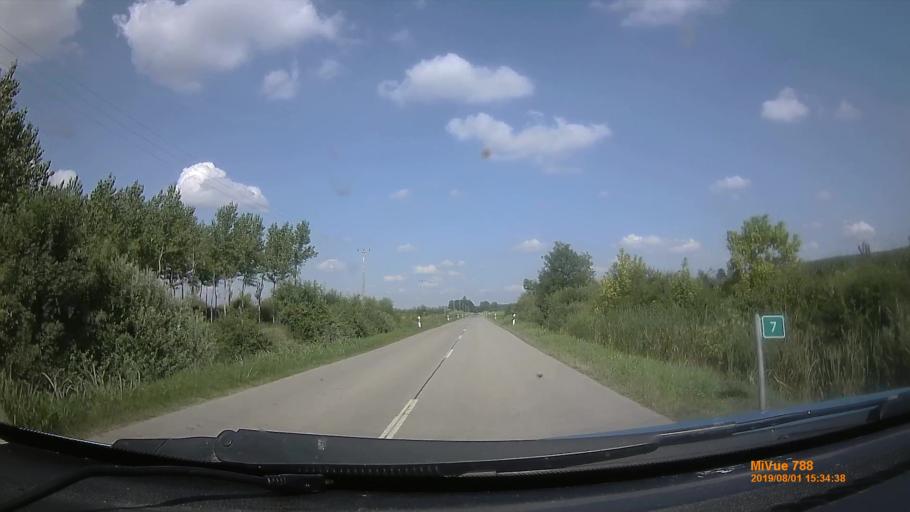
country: HU
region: Baranya
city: Sellye
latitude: 45.9584
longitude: 17.8984
